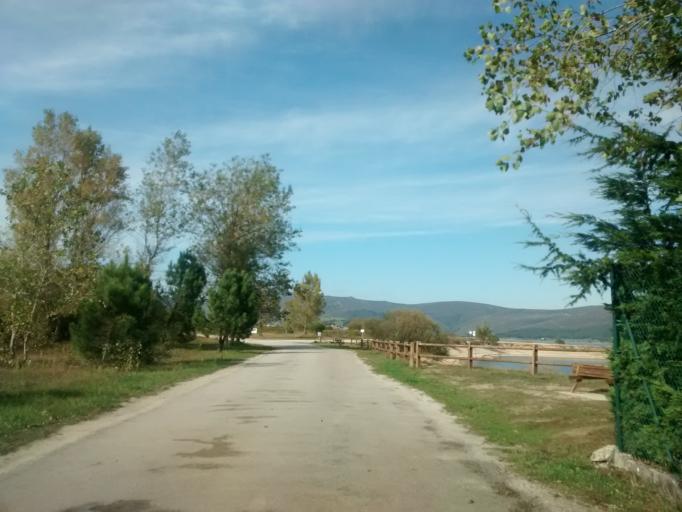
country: ES
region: Castille and Leon
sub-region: Provincia de Burgos
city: Arija
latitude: 43.0022
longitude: -3.9450
